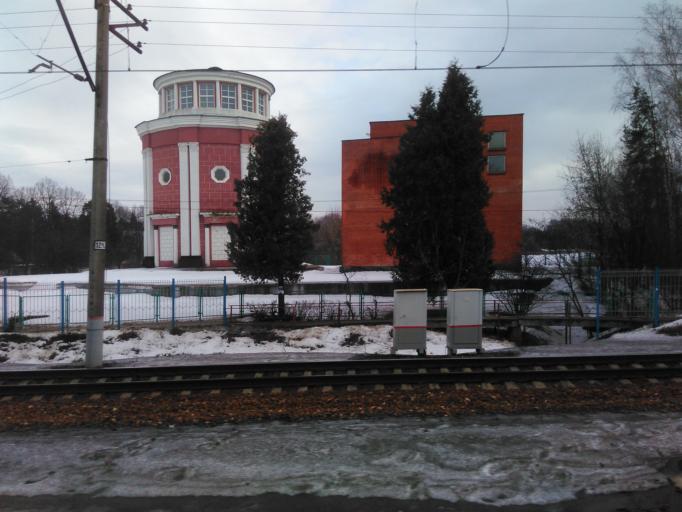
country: RU
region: Moskovskaya
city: Cherkizovo
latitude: 55.9495
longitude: 37.8010
